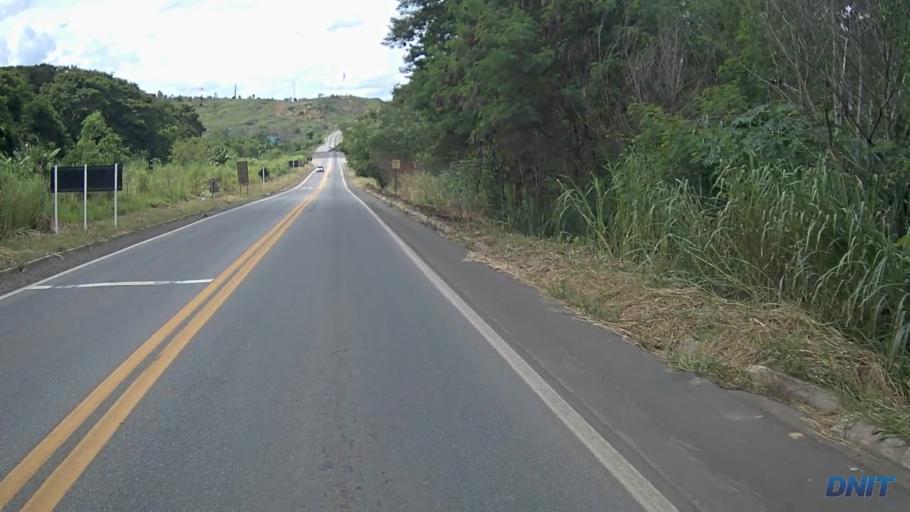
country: BR
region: Minas Gerais
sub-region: Ipatinga
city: Ipatinga
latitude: -19.4429
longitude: -42.5127
